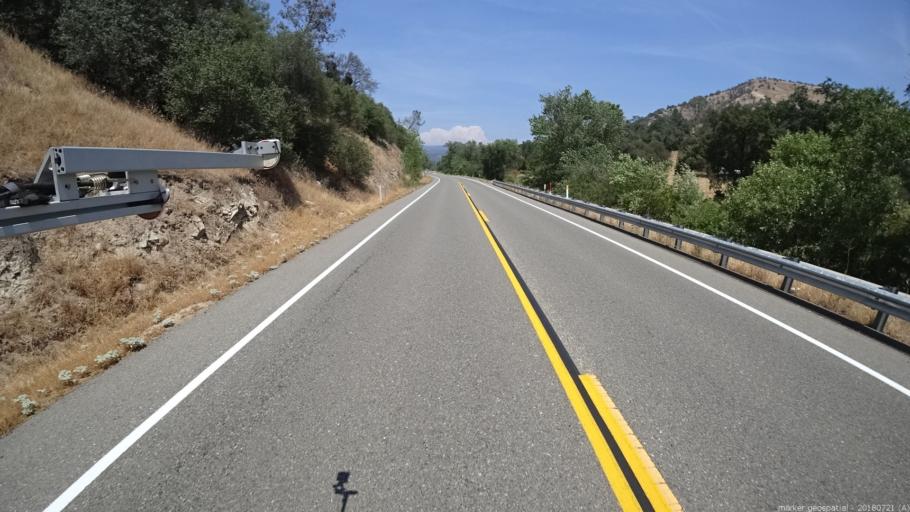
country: US
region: California
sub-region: Madera County
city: Coarsegold
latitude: 37.1728
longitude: -119.6342
